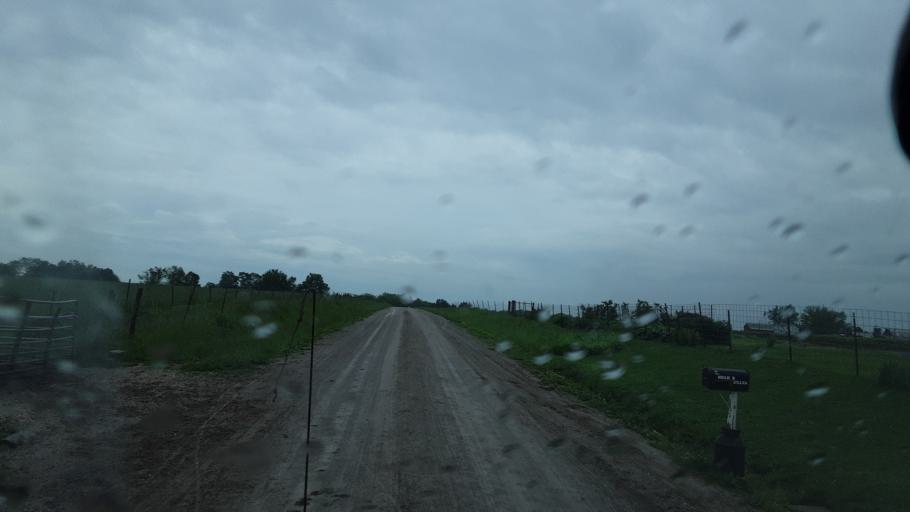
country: US
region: Missouri
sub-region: Randolph County
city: Moberly
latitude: 39.3079
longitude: -92.3053
